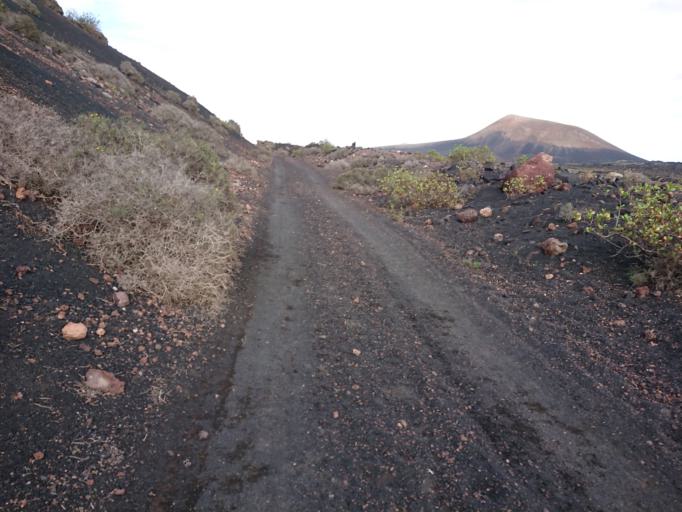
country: ES
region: Canary Islands
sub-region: Provincia de Las Palmas
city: Tinajo
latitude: 29.0116
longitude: -13.6938
